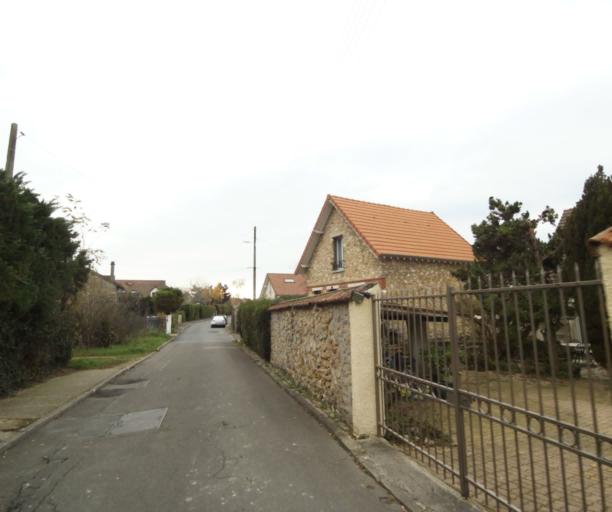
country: FR
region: Ile-de-France
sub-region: Departement des Yvelines
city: Triel-sur-Seine
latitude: 48.9809
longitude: 2.0167
